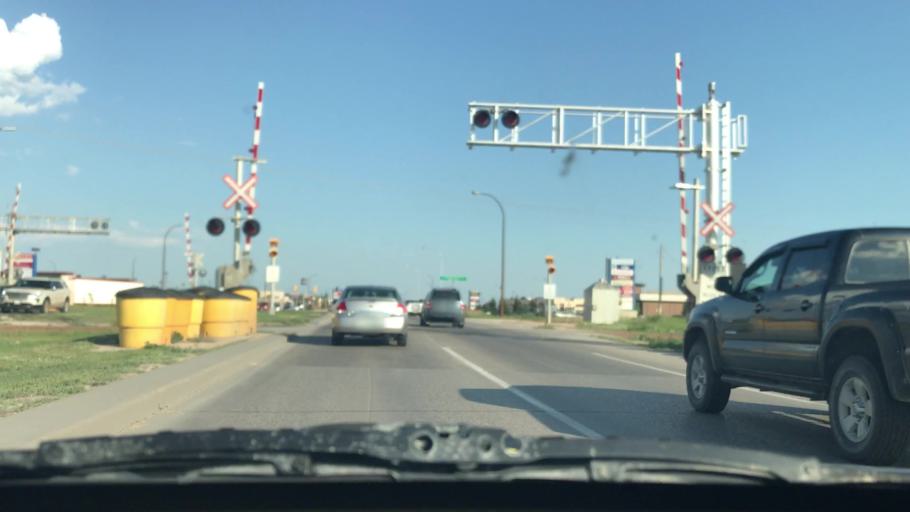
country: CA
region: Manitoba
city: Winnipeg
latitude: 49.8276
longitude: -97.2076
